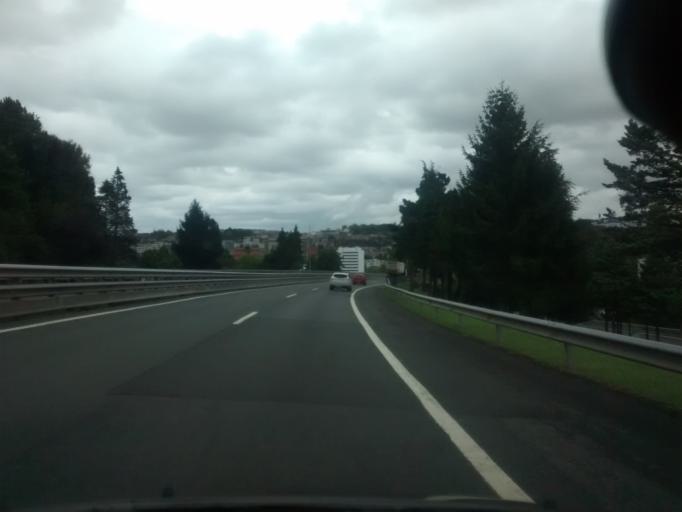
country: ES
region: Basque Country
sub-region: Provincia de Guipuzcoa
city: Lasarte
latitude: 43.2981
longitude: -2.0092
